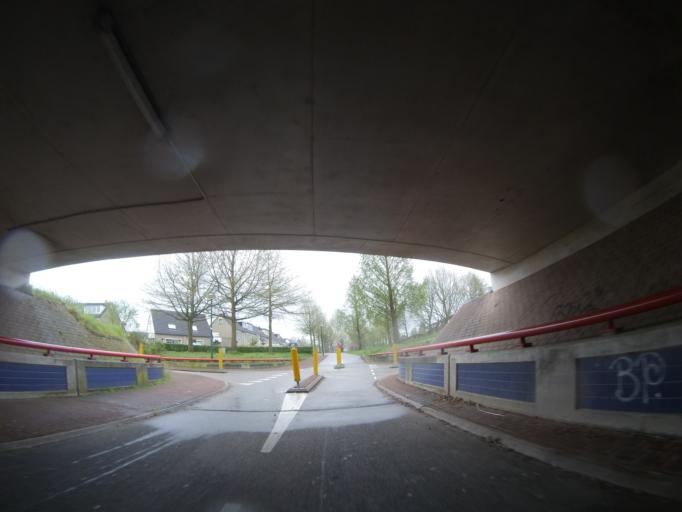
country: NL
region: Utrecht
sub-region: Gemeente Leusden
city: Leusden
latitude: 52.1427
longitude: 5.4301
